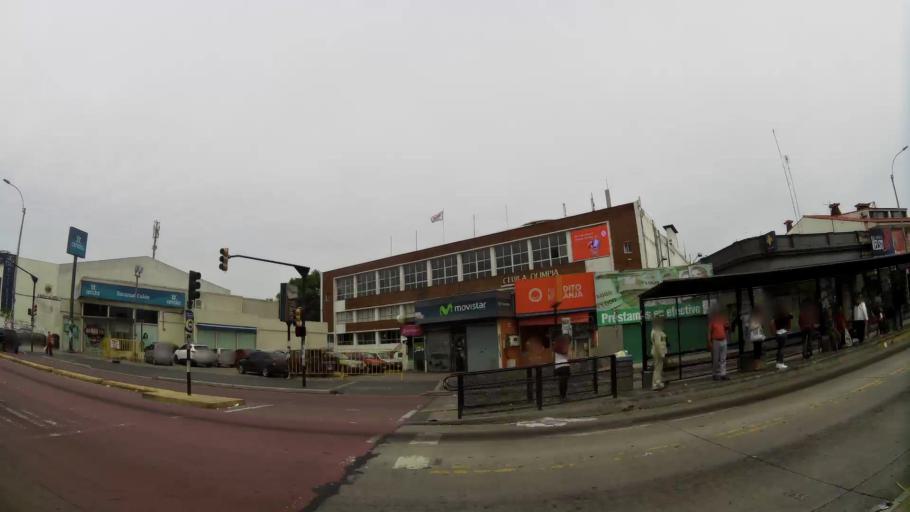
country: UY
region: Canelones
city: La Paz
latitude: -34.8056
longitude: -56.2222
